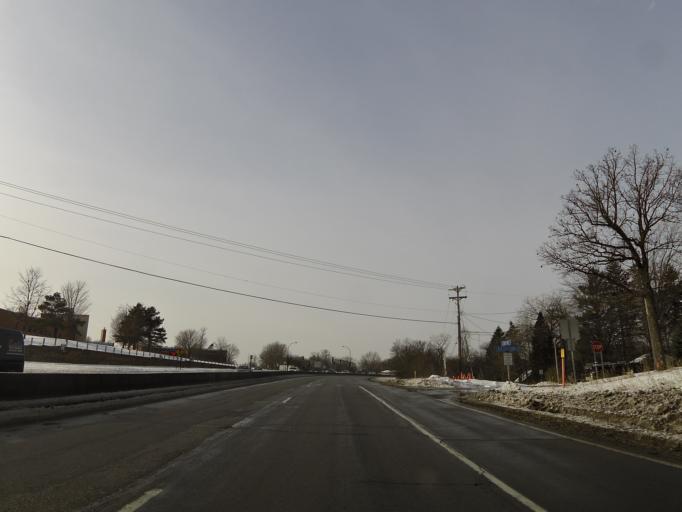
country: US
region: Minnesota
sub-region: Hennepin County
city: Minnetonka
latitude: 44.9115
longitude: -93.5094
